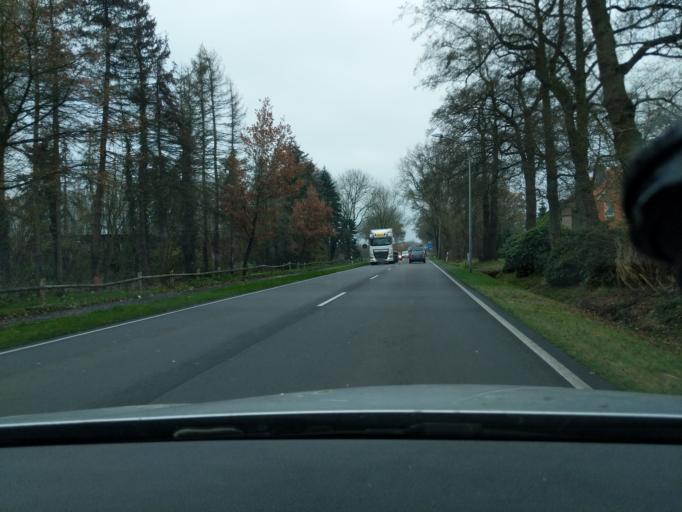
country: DE
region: Lower Saxony
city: Gyhum
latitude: 53.2005
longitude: 9.2883
